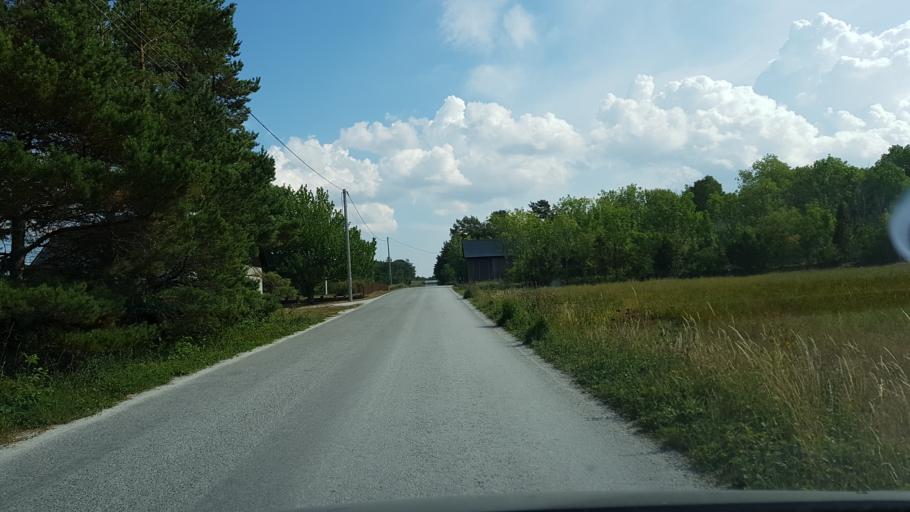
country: SE
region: Gotland
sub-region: Gotland
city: Visby
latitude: 57.8215
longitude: 18.5169
